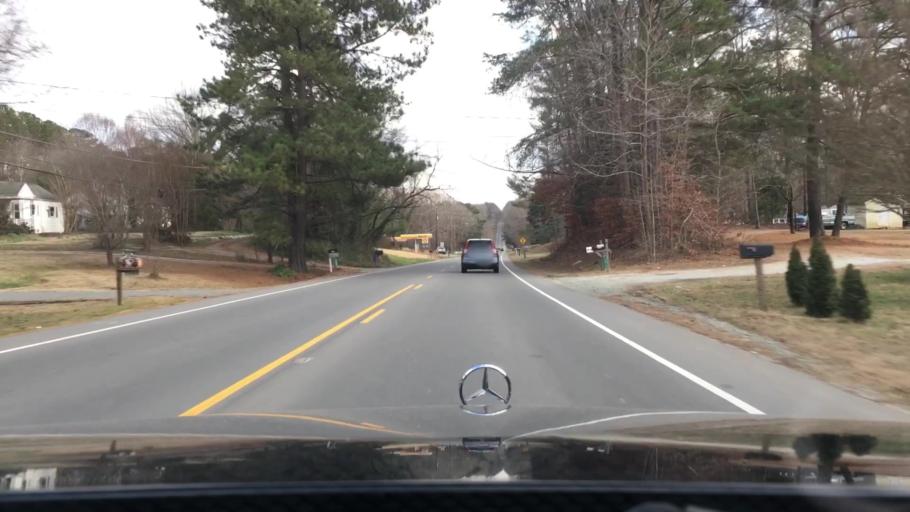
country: US
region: North Carolina
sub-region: Orange County
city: Hillsborough
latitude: 36.0806
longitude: -79.0774
